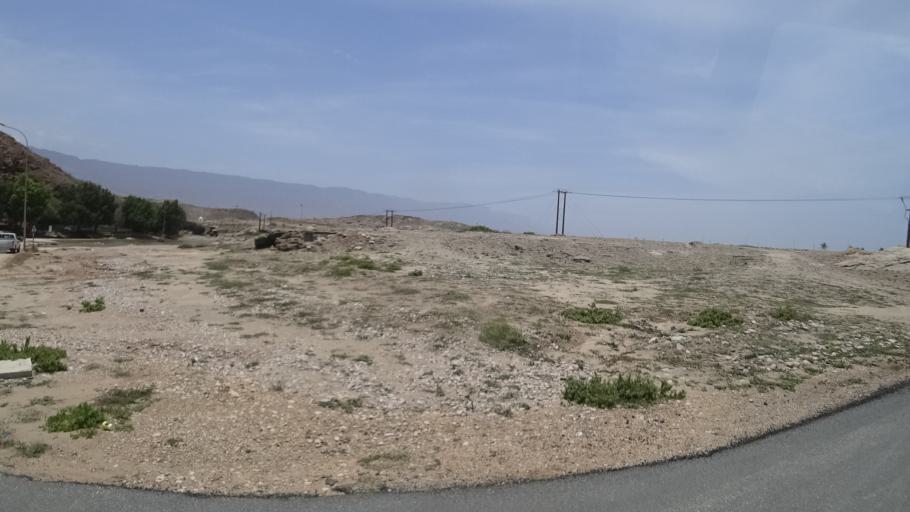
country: OM
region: Zufar
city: Salalah
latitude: 16.9993
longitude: 54.6916
